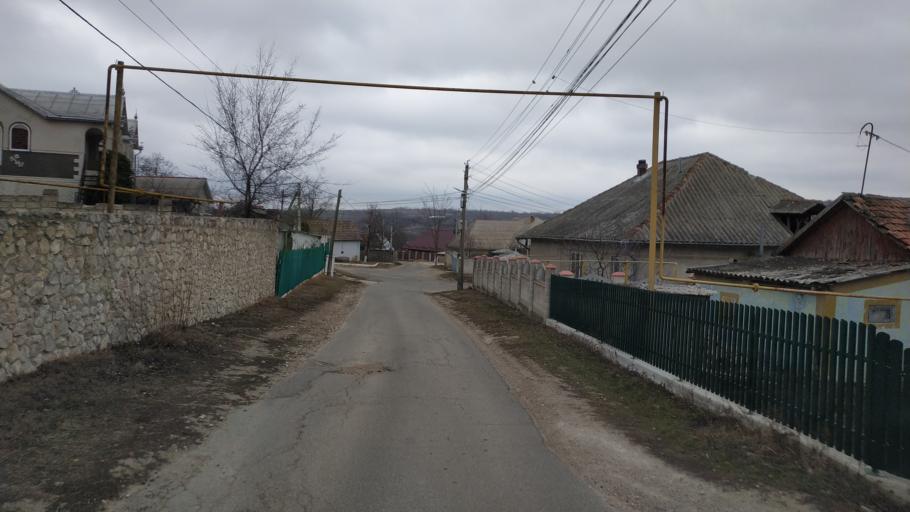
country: MD
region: Laloveni
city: Ialoveni
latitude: 46.9020
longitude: 28.8011
